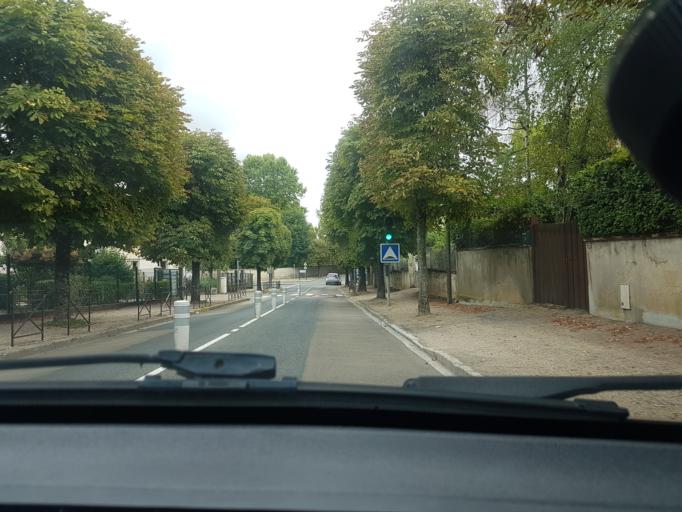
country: FR
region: Bourgogne
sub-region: Departement de l'Yonne
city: Auxerre
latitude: 47.8036
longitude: 3.5733
